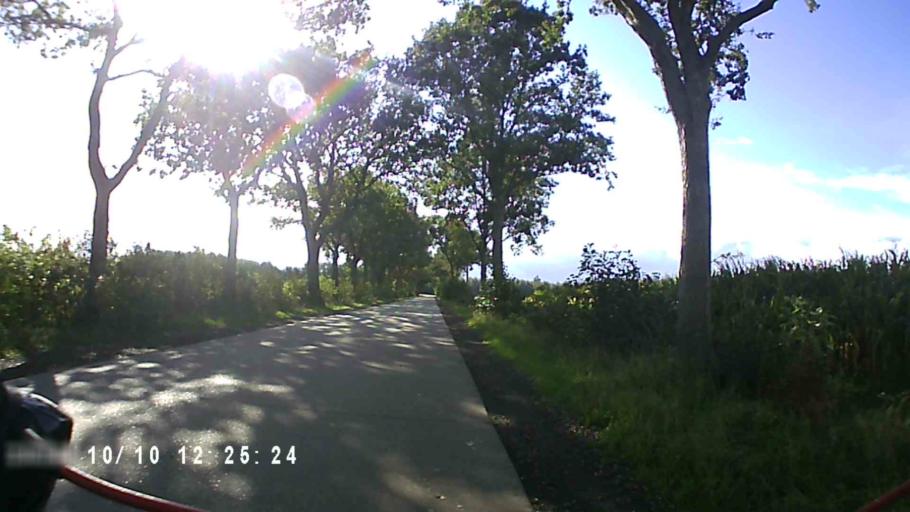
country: NL
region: Friesland
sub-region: Gemeente Heerenveen
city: Jubbega
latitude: 52.9892
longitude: 6.1799
